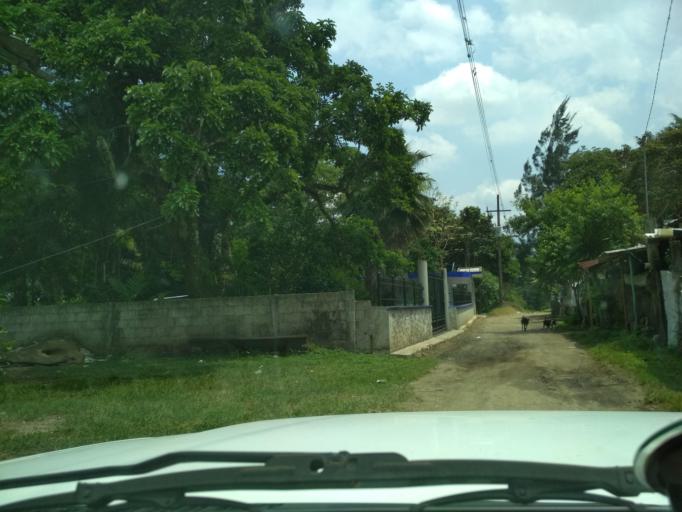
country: MX
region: Veracruz
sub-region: Ixtaczoquitlan
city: Buenavista
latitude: 18.8847
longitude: -97.0477
